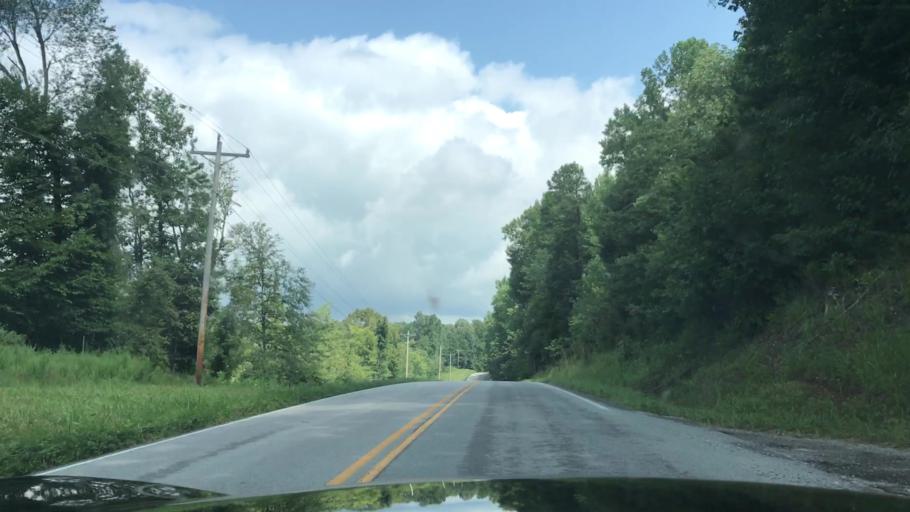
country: US
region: Kentucky
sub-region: Ohio County
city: Oak Grove
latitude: 37.1967
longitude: -86.8848
